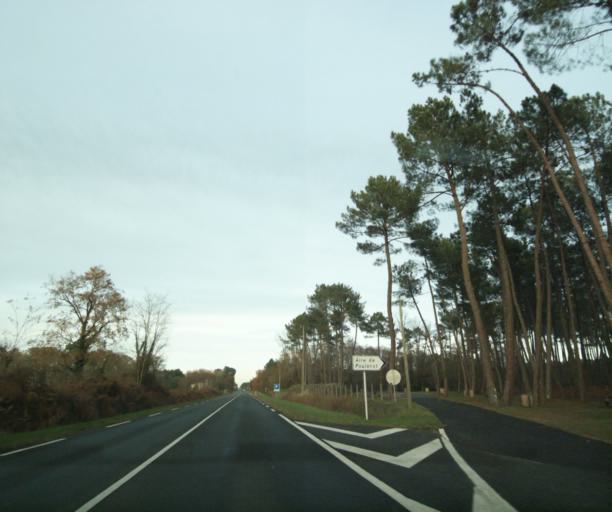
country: FR
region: Aquitaine
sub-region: Departement de la Gironde
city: Bazas
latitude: 44.3105
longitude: -0.2501
